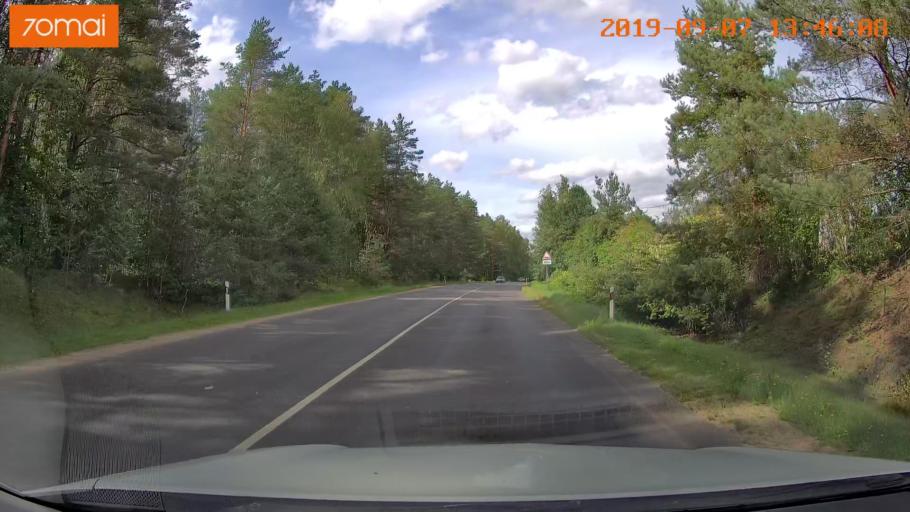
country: LT
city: Baltoji Voke
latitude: 54.5894
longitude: 25.2359
